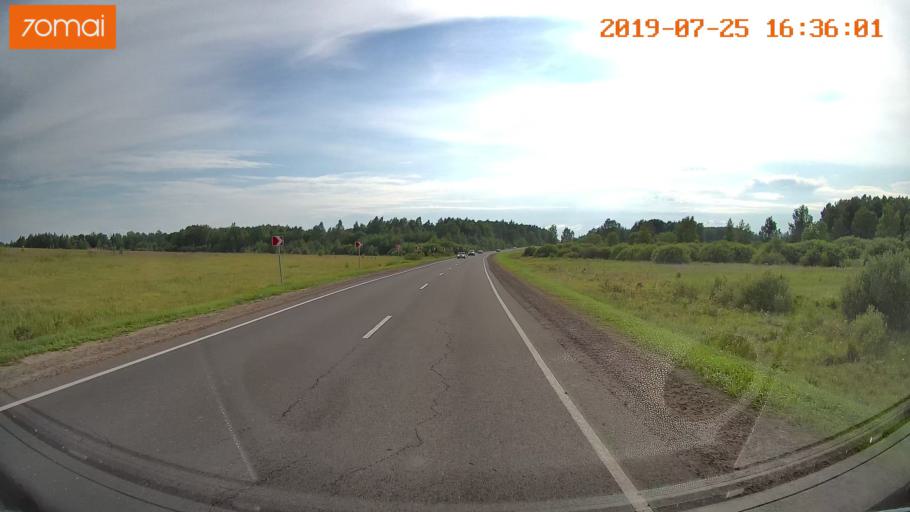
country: RU
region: Ivanovo
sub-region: Privolzhskiy Rayon
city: Ples
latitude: 57.3992
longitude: 41.4121
